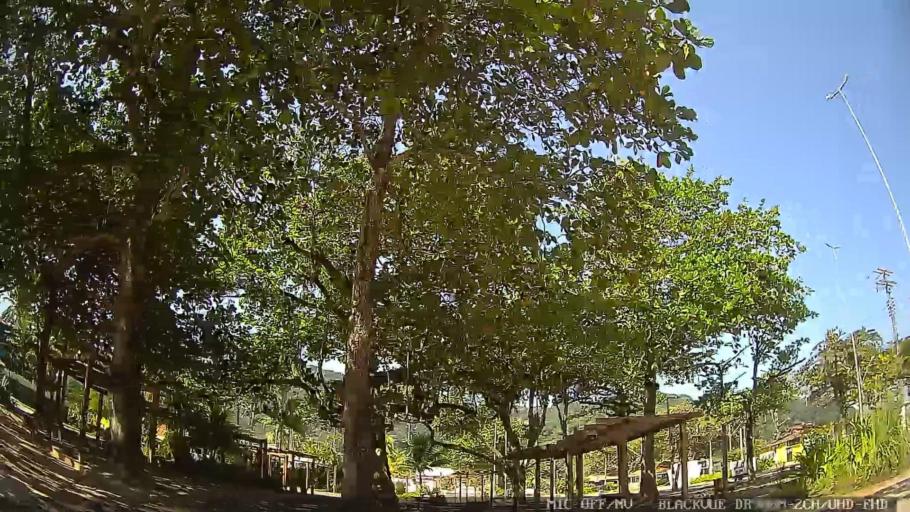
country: BR
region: Sao Paulo
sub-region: Guaruja
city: Guaruja
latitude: -24.0191
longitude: -46.2969
